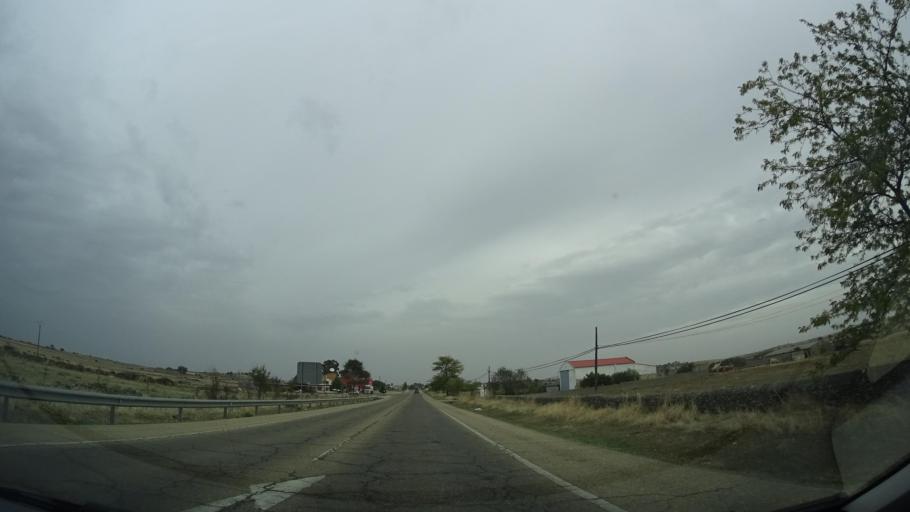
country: ES
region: Extremadura
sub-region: Provincia de Caceres
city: Trujillo
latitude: 39.4672
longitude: -5.8639
